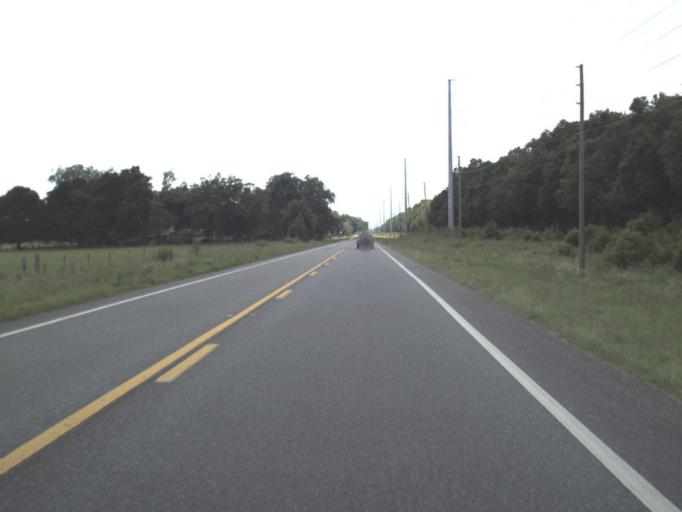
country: US
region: Florida
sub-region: Gilchrist County
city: Trenton
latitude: 29.6121
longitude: -82.9085
